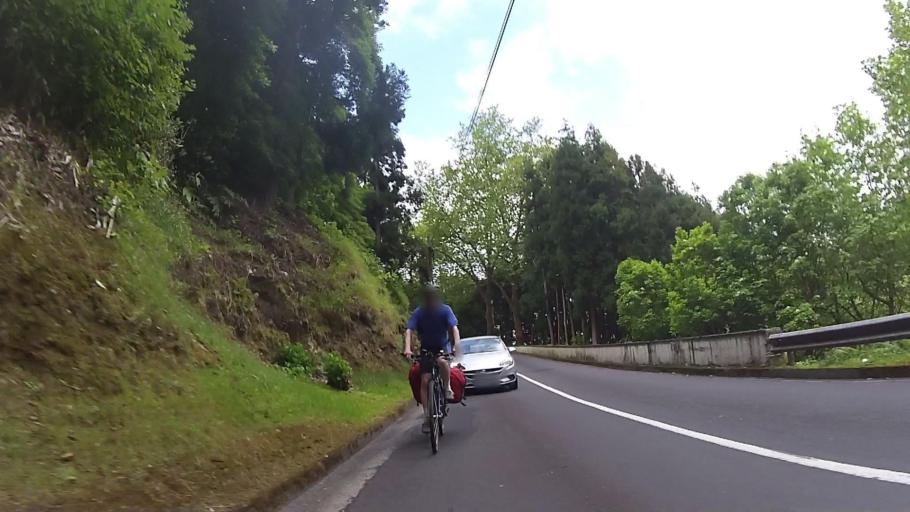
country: PT
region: Azores
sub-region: Povoacao
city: Furnas
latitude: 37.7632
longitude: -25.2860
